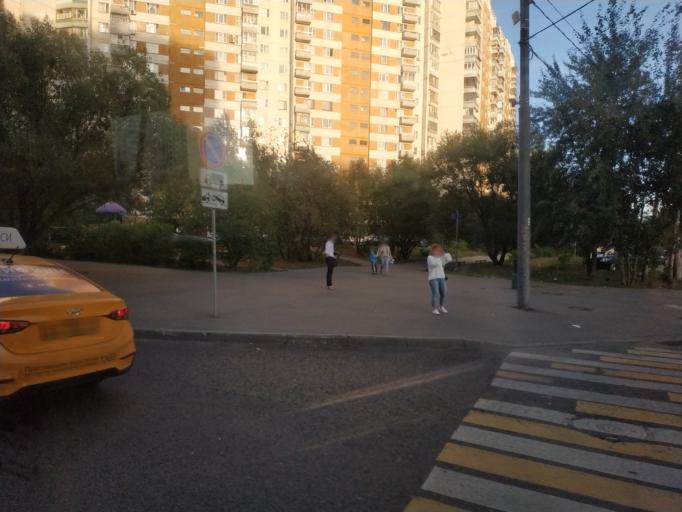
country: RU
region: Moscow
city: Novo-Peredelkino
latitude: 55.6456
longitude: 37.3399
